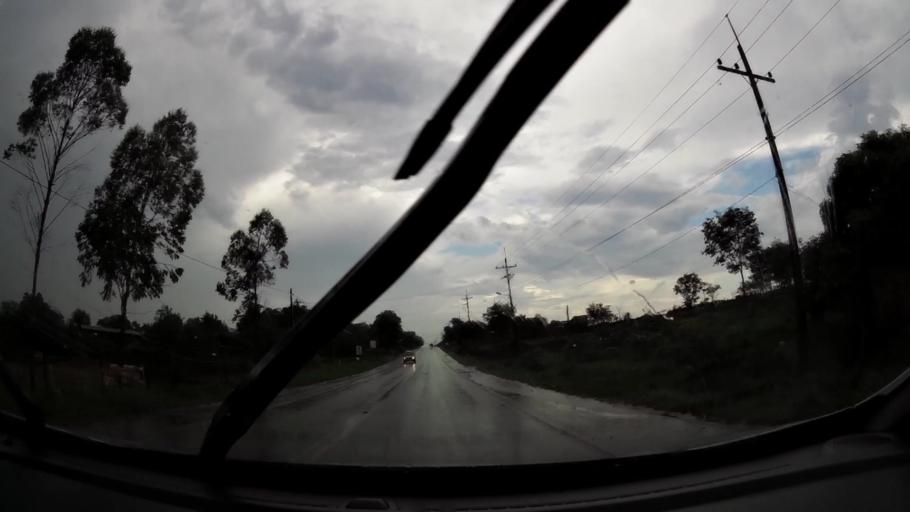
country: PY
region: Alto Parana
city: Presidente Franco
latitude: -25.5647
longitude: -54.6668
